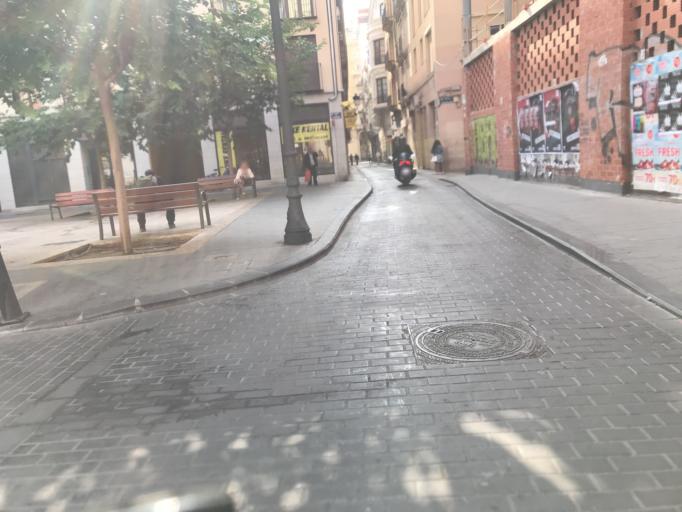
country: ES
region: Valencia
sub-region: Provincia de Valencia
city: Valencia
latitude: 39.4722
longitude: -0.3789
